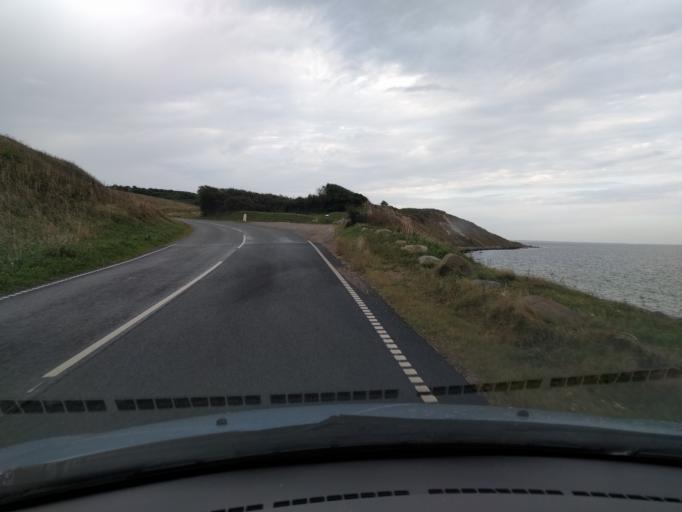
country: DK
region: South Denmark
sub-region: Assens Kommune
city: Assens
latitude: 55.1752
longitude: 9.9855
